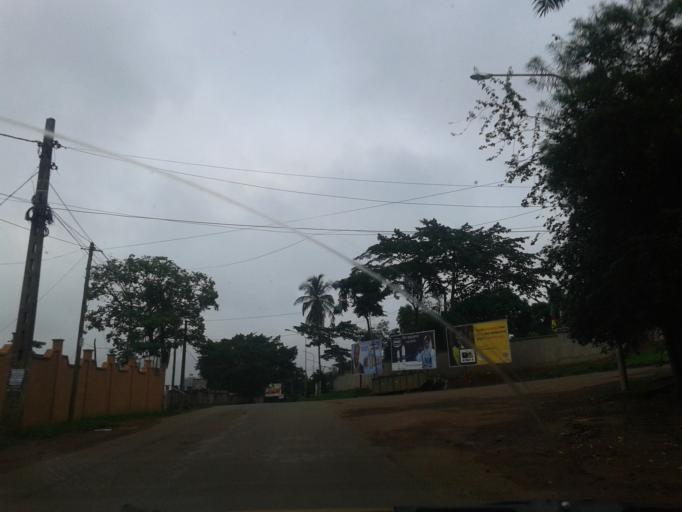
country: CM
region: Centre
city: Yaounde
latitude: 3.8720
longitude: 11.5191
